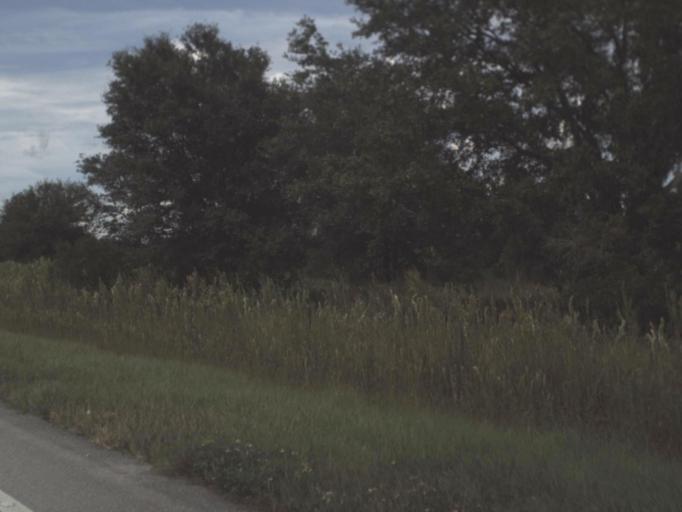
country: US
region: Florida
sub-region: Highlands County
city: Placid Lakes
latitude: 27.2089
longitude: -81.4865
